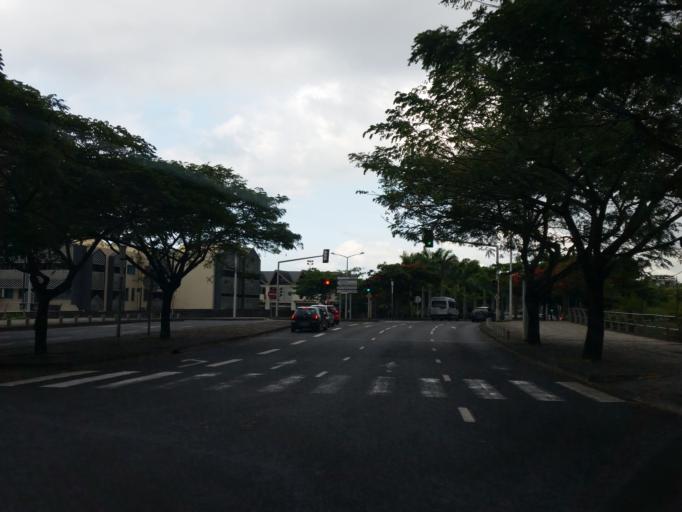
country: RE
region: Reunion
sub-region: Reunion
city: Saint-Denis
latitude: -20.8899
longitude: 55.4639
